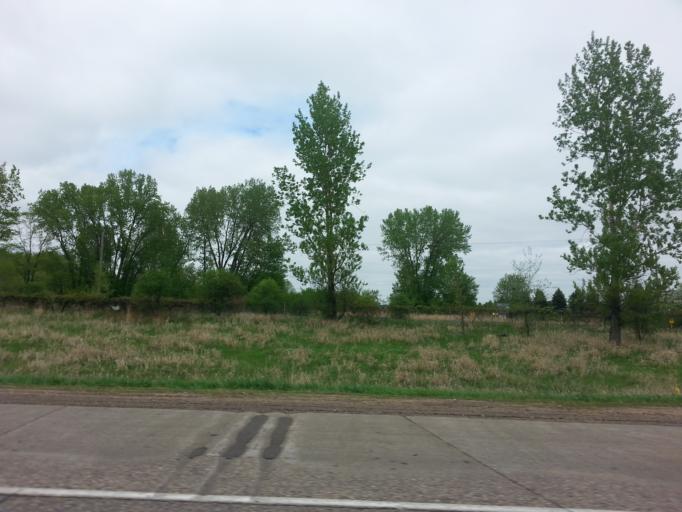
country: US
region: Minnesota
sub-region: Washington County
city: Lake Elmo
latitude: 44.9488
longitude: -92.8731
